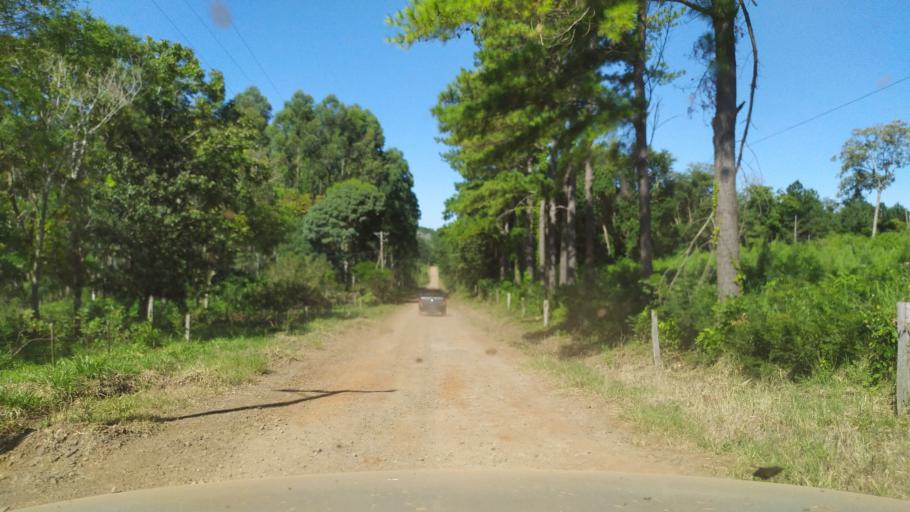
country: AR
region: Misiones
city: Caraguatay
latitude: -26.6813
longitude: -54.7080
